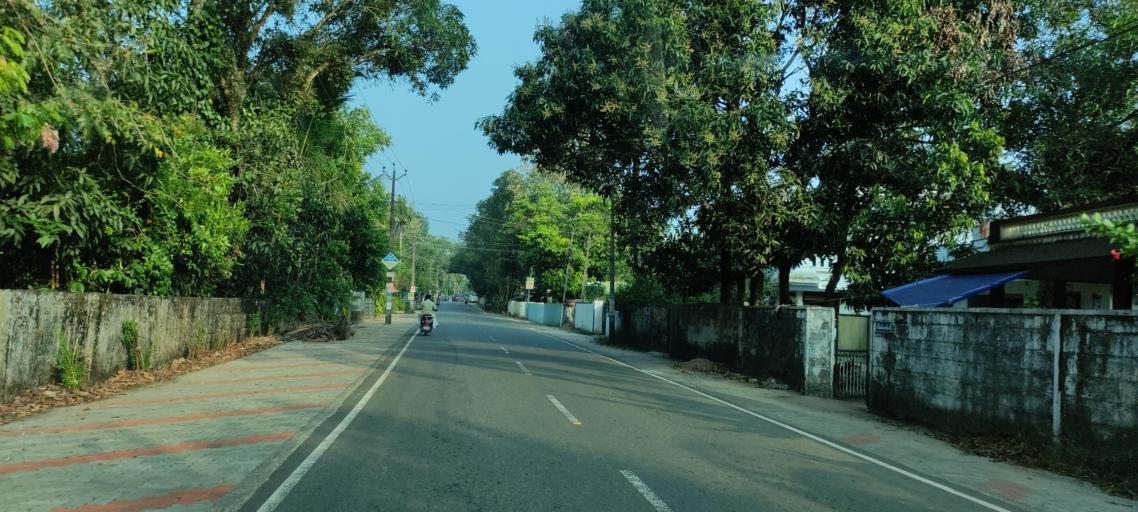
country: IN
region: Kerala
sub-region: Alappuzha
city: Shertallai
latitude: 9.6544
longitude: 76.3410
